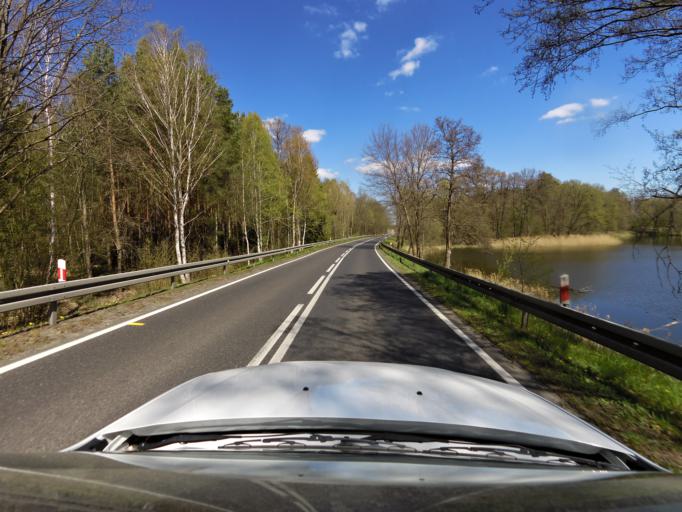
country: PL
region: West Pomeranian Voivodeship
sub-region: Powiat mysliborski
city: Debno
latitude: 52.7776
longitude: 14.7512
